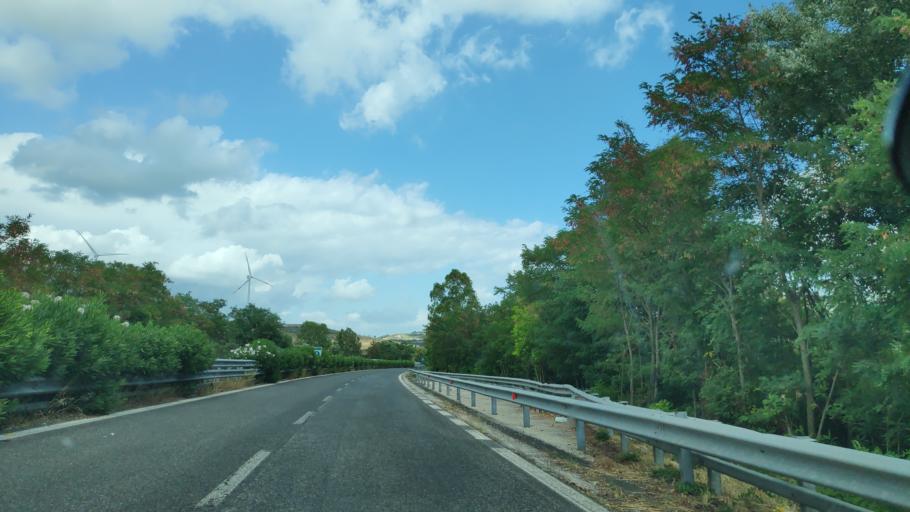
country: IT
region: Campania
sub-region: Provincia di Salerno
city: Serre
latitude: 40.6168
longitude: 15.1647
